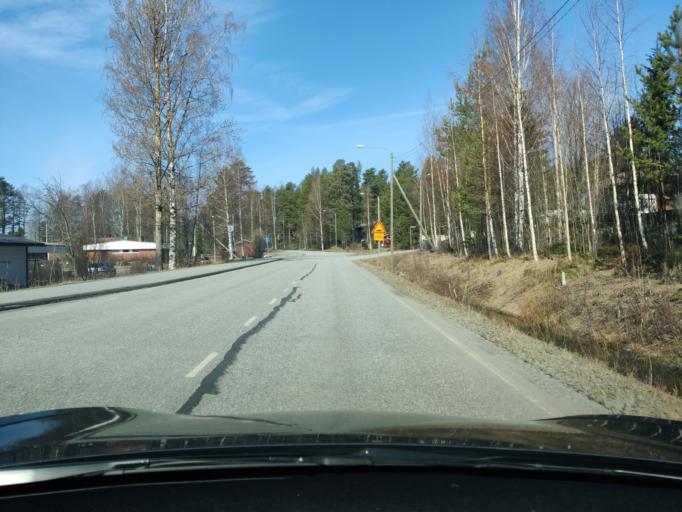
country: FI
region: Northern Savo
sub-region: Kuopio
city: Vehmersalmi
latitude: 62.7659
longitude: 28.0185
